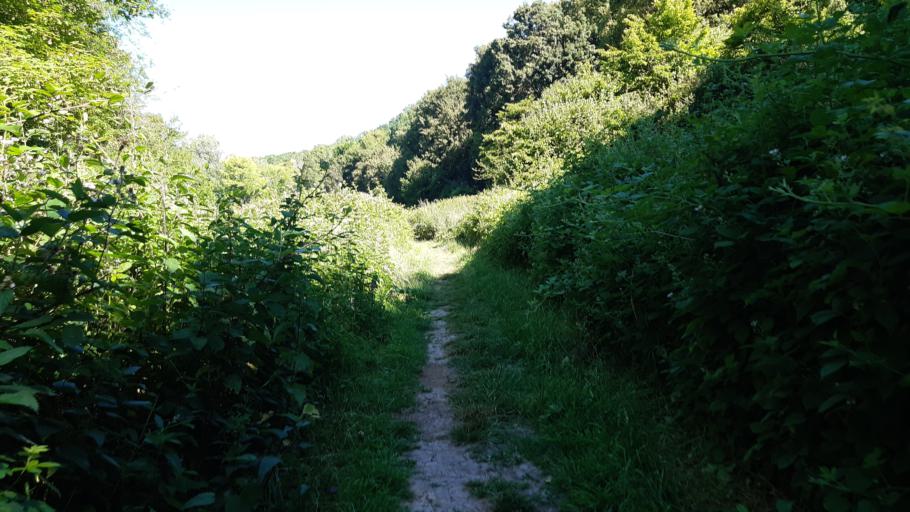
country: FR
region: Centre
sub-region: Departement d'Indre-et-Loire
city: Mettray
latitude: 47.4362
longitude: 0.6601
